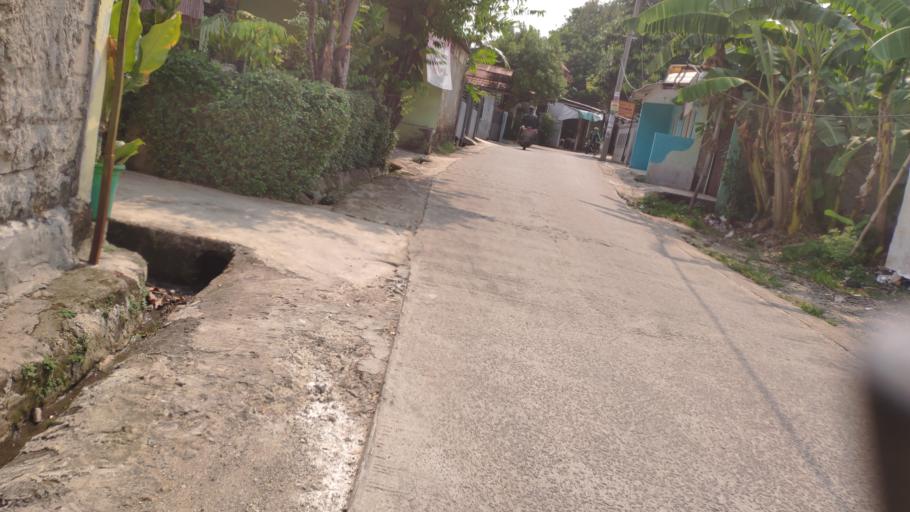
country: ID
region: West Java
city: Depok
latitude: -6.3829
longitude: 106.7987
